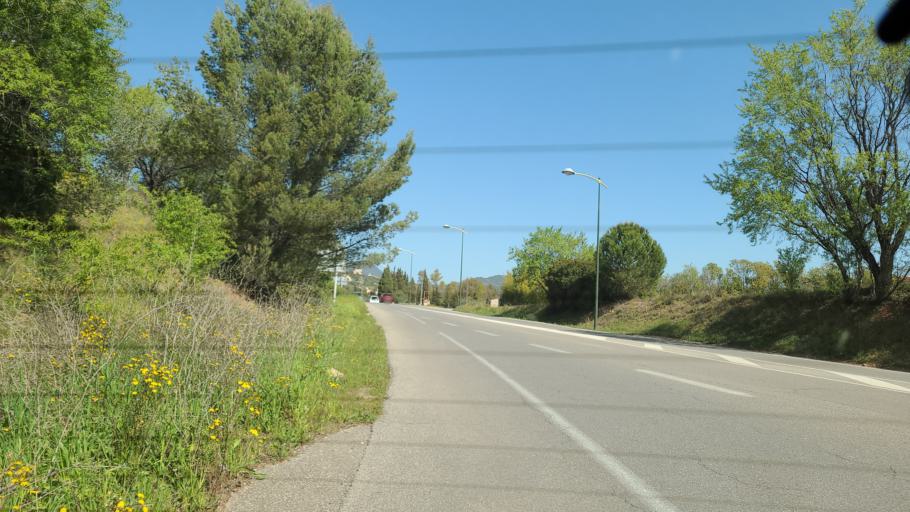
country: FR
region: Provence-Alpes-Cote d'Azur
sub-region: Departement du Var
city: Cuers
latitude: 43.2240
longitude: 6.0702
